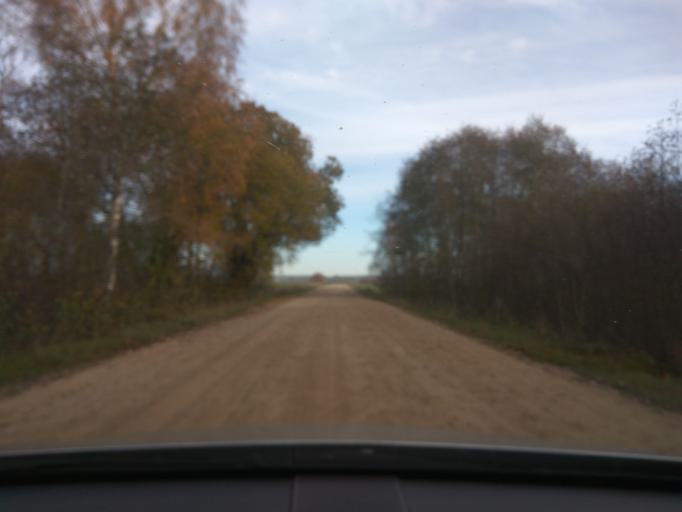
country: LV
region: Aizpute
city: Aizpute
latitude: 56.8490
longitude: 21.6641
